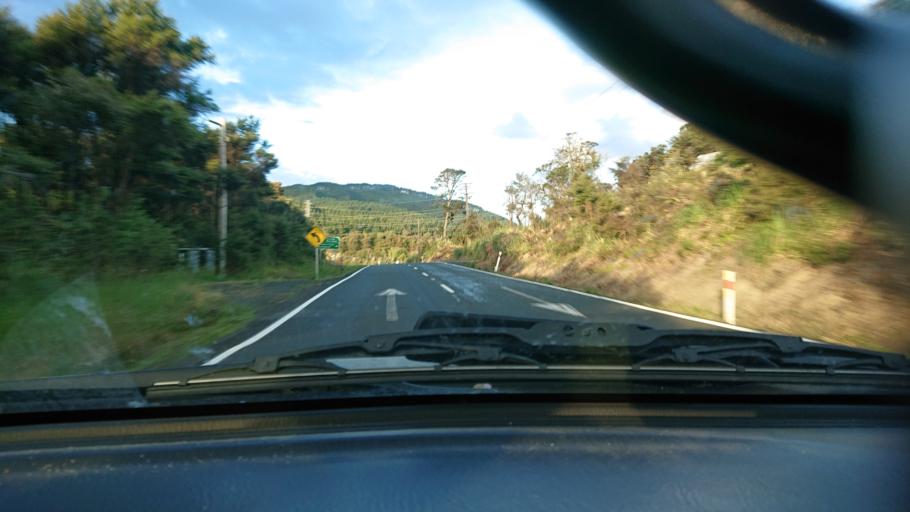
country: NZ
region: Auckland
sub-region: Auckland
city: Parakai
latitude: -36.5092
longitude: 174.4556
